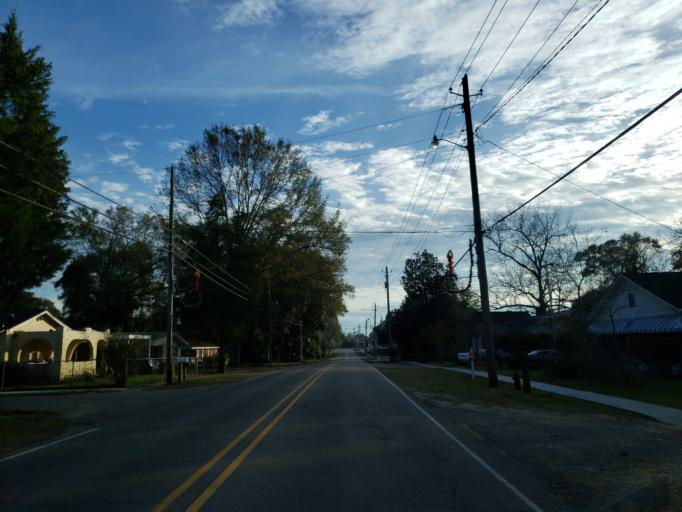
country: US
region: Mississippi
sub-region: Lamar County
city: Purvis
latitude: 31.1474
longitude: -89.4118
